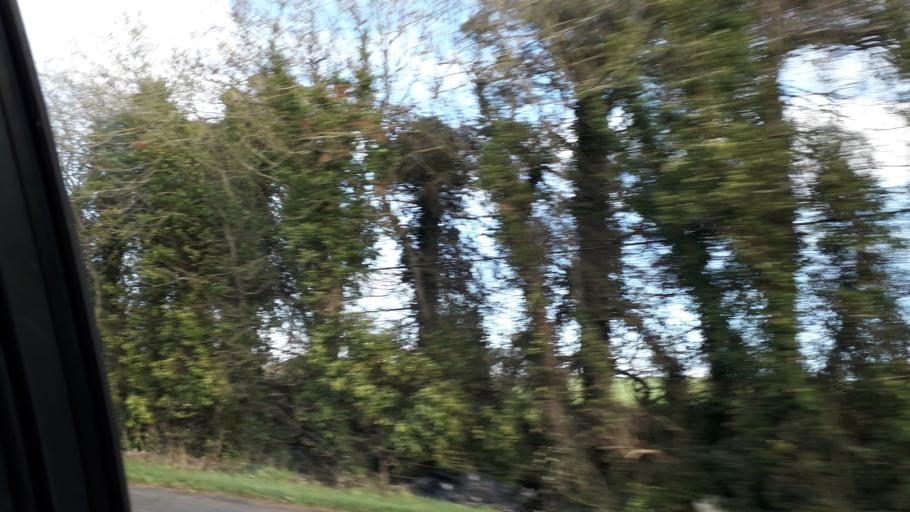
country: IE
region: Leinster
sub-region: An Mhi
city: Slane
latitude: 53.6886
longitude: -6.5414
